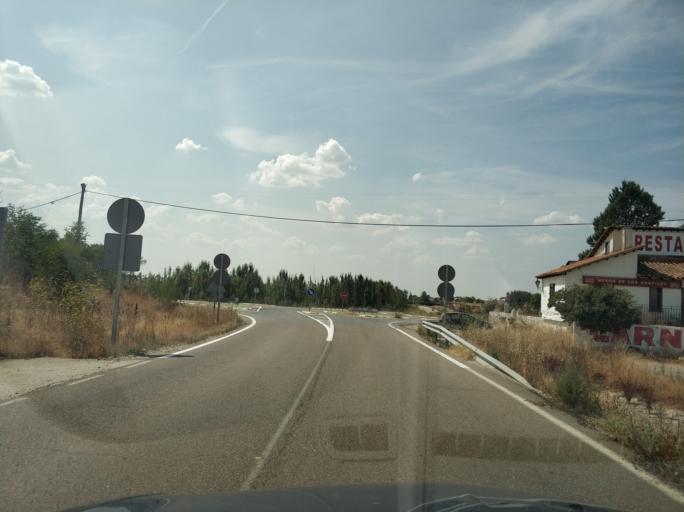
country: ES
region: Castille and Leon
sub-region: Provincia de Salamanca
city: Arapiles
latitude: 40.8956
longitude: -5.6634
